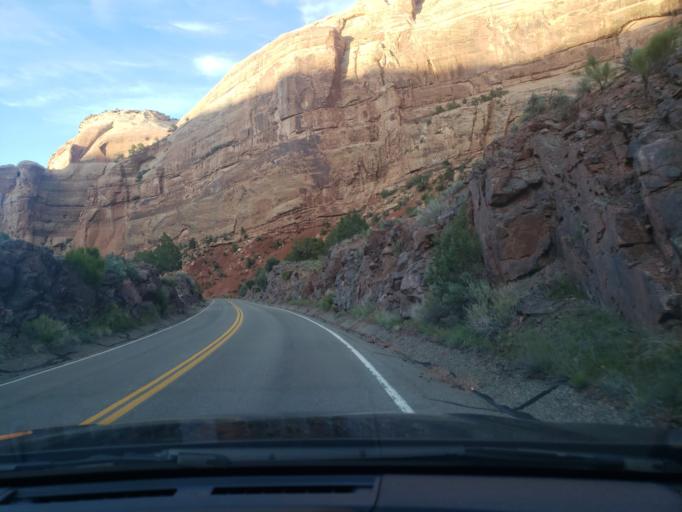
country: US
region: Colorado
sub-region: Mesa County
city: Fruita
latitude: 39.1098
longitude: -108.7330
